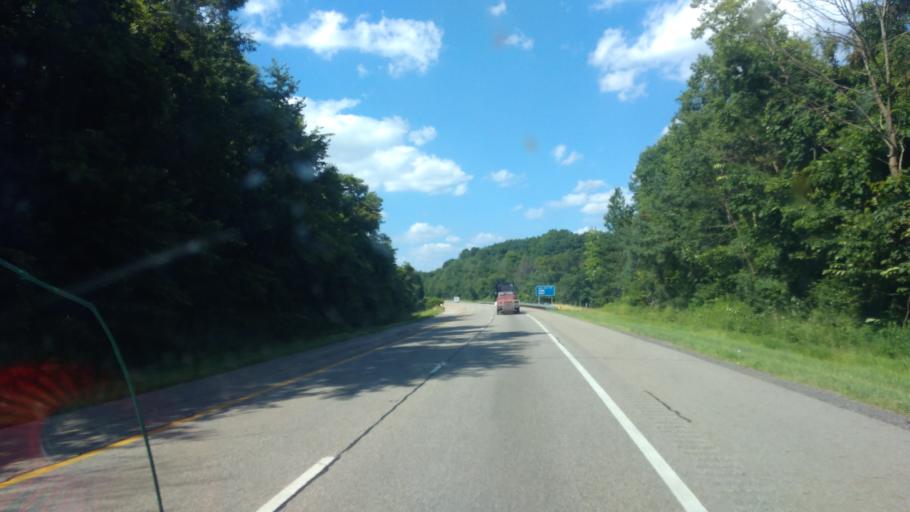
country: US
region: Ohio
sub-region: Stark County
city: Richville
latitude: 40.7129
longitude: -81.4222
